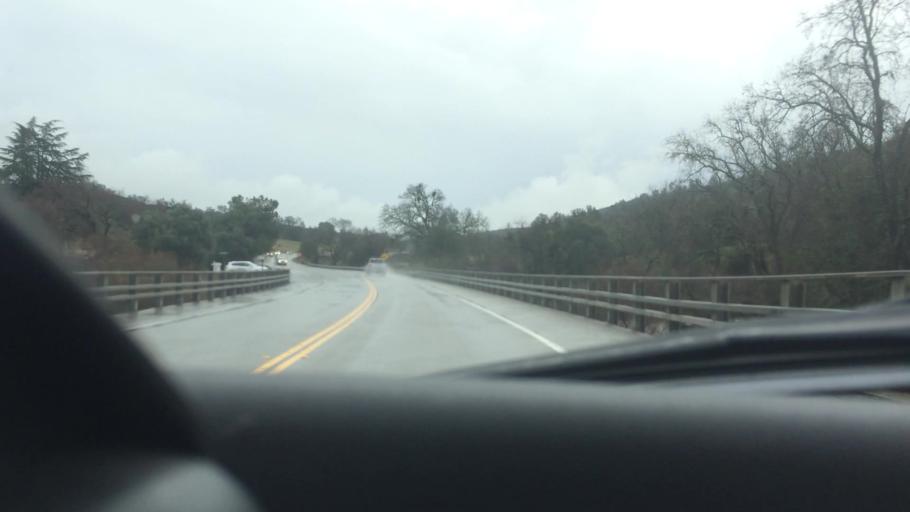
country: US
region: California
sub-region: El Dorado County
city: Cameron Park
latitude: 38.6008
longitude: -121.0233
